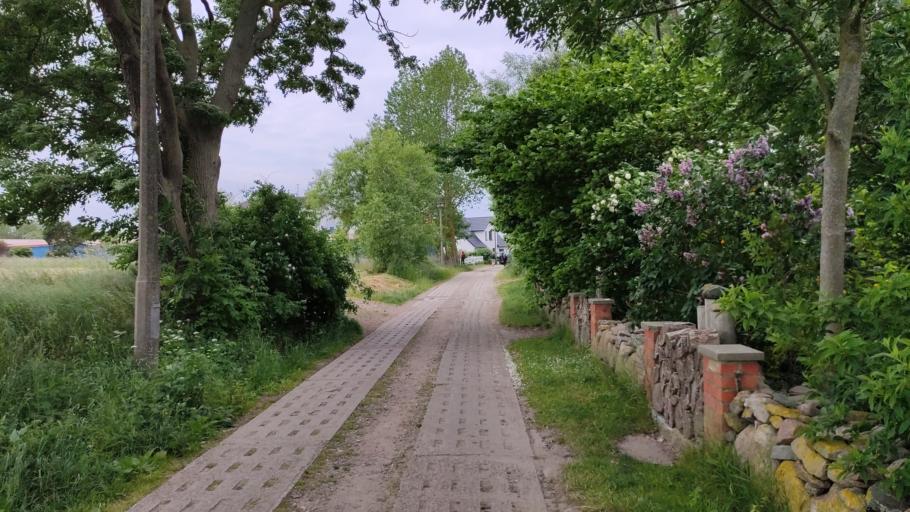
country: DE
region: Mecklenburg-Vorpommern
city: Bastorf
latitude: 54.1359
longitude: 11.6579
